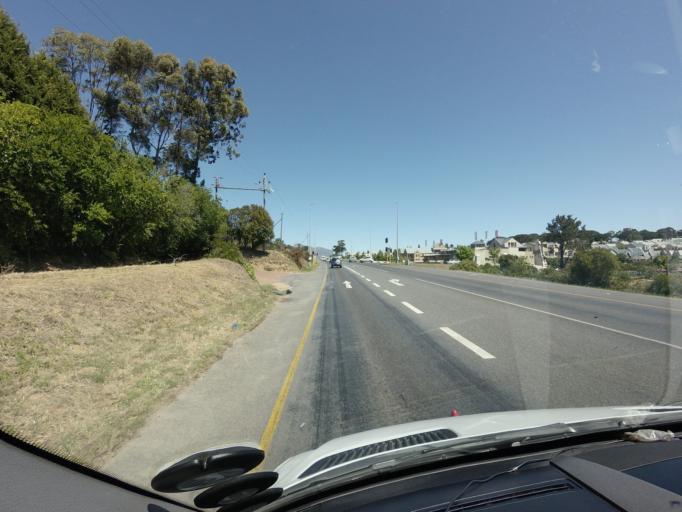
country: ZA
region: Western Cape
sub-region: Cape Winelands District Municipality
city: Stellenbosch
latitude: -33.9003
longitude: 18.8589
